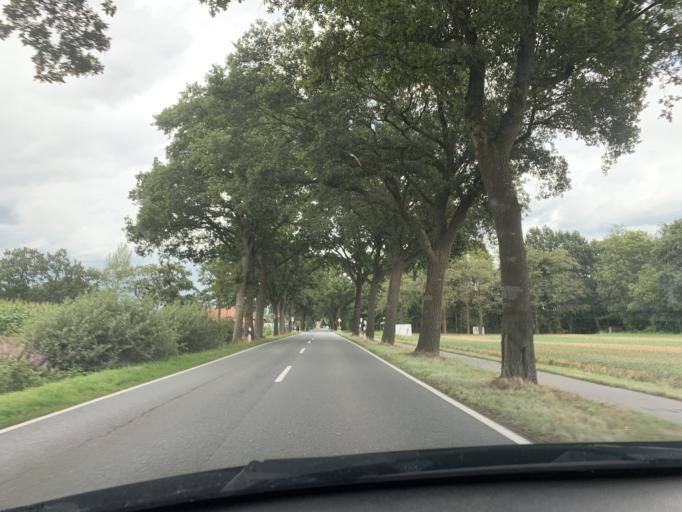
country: DE
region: Lower Saxony
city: Westerstede
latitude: 53.2412
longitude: 7.9193
